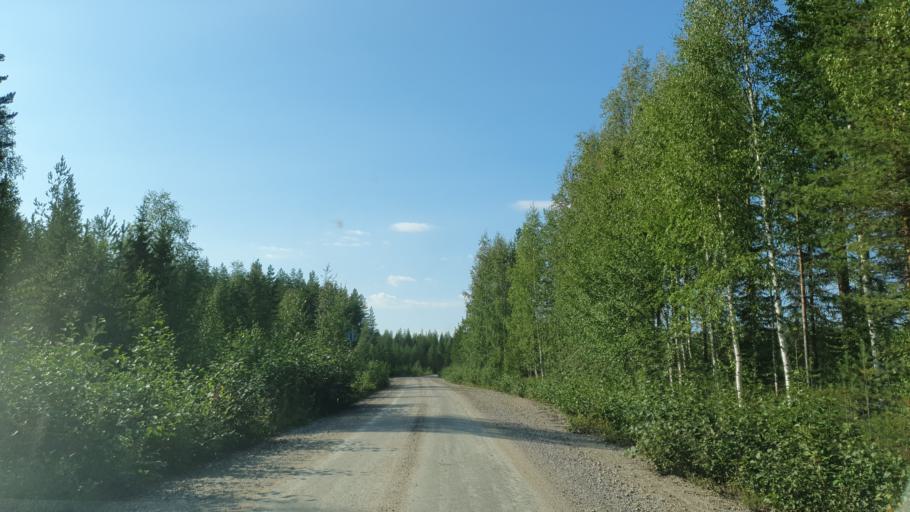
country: FI
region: Kainuu
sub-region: Kehys-Kainuu
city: Kuhmo
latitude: 64.1100
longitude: 29.5836
